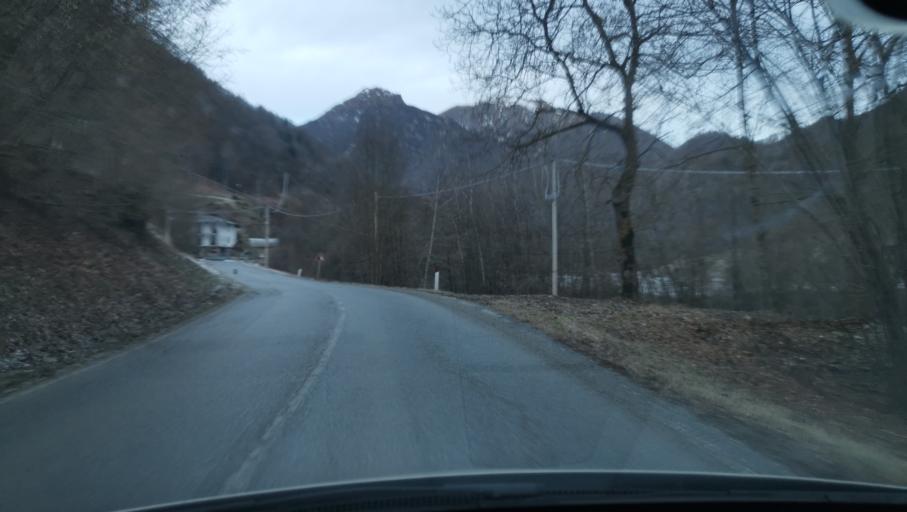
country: IT
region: Piedmont
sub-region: Provincia di Cuneo
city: Pradleves
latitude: 44.4113
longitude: 7.2959
